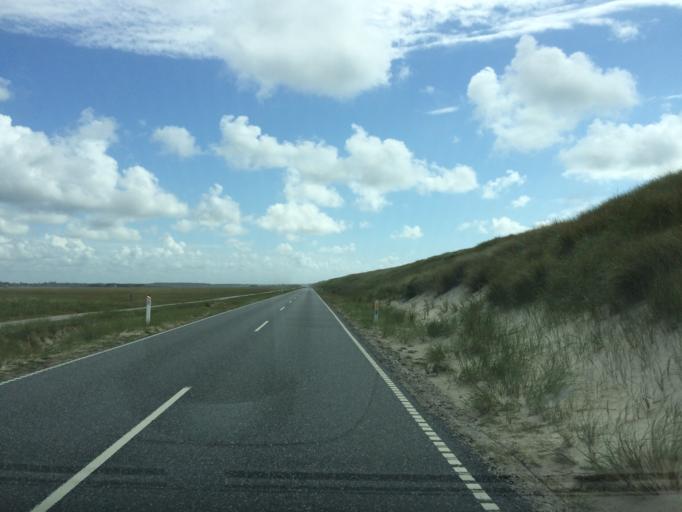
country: DK
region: Central Jutland
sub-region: Holstebro Kommune
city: Ulfborg
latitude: 56.3498
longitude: 8.1224
